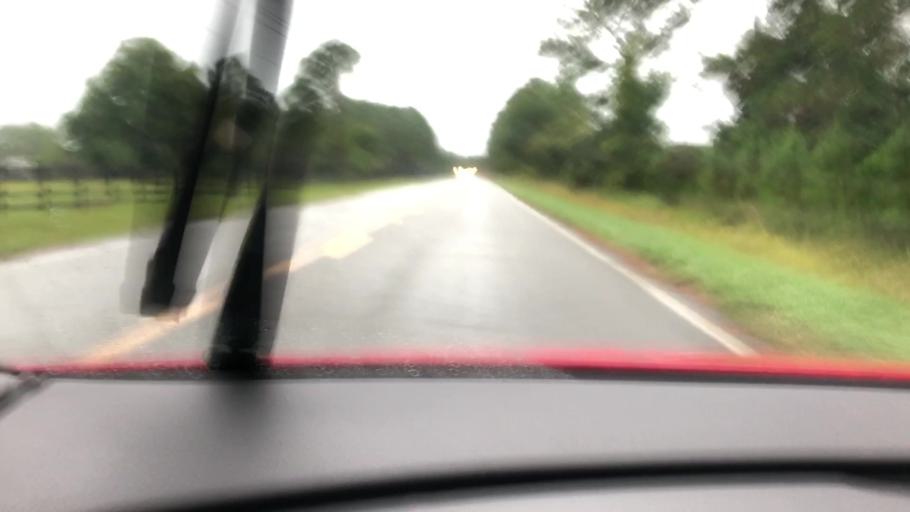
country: US
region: Florida
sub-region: Volusia County
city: Samsula-Spruce Creek
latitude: 29.0268
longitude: -81.1084
